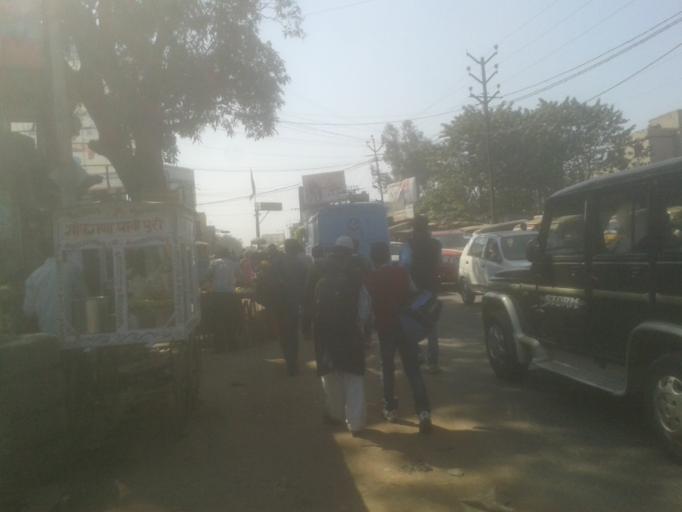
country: IN
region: Jharkhand
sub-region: Ranchi
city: Ranchi
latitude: 23.3649
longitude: 85.3457
